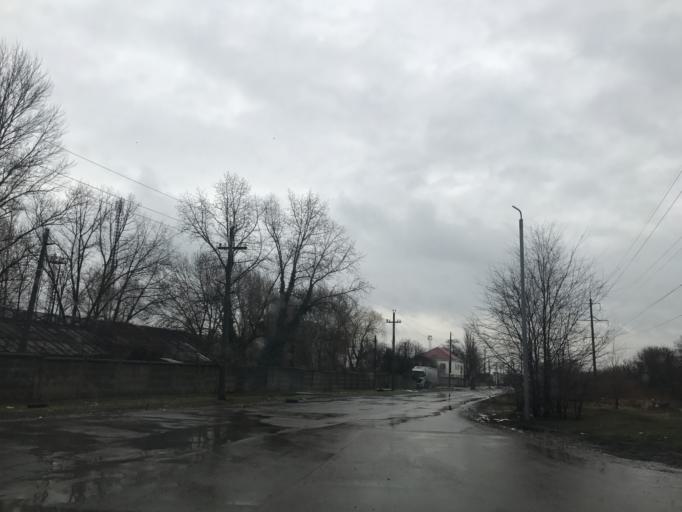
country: RU
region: Rostov
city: Severnyy
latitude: 47.2458
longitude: 39.6223
